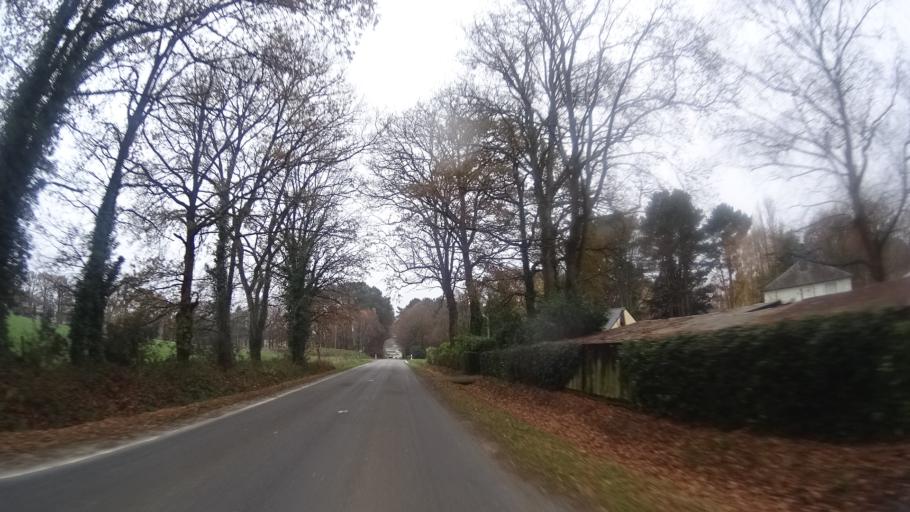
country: FR
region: Brittany
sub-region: Departement d'Ille-et-Vilaine
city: Bains-sur-Oust
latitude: 47.6950
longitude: -2.0568
